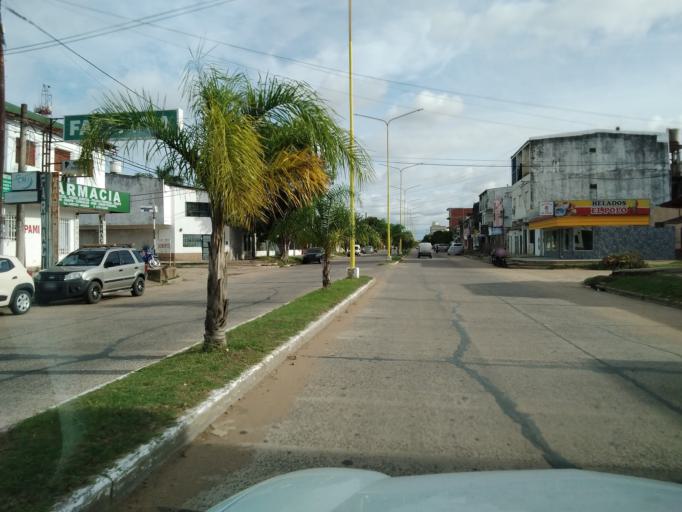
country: AR
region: Corrientes
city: Corrientes
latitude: -27.4623
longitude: -58.7872
